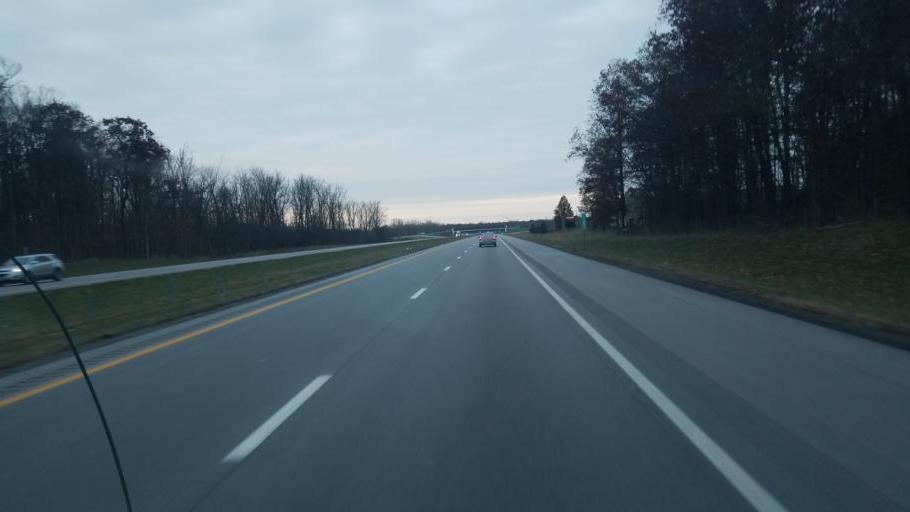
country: US
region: Ohio
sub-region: Allen County
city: Fort Shawnee
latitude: 40.6925
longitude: -84.1172
